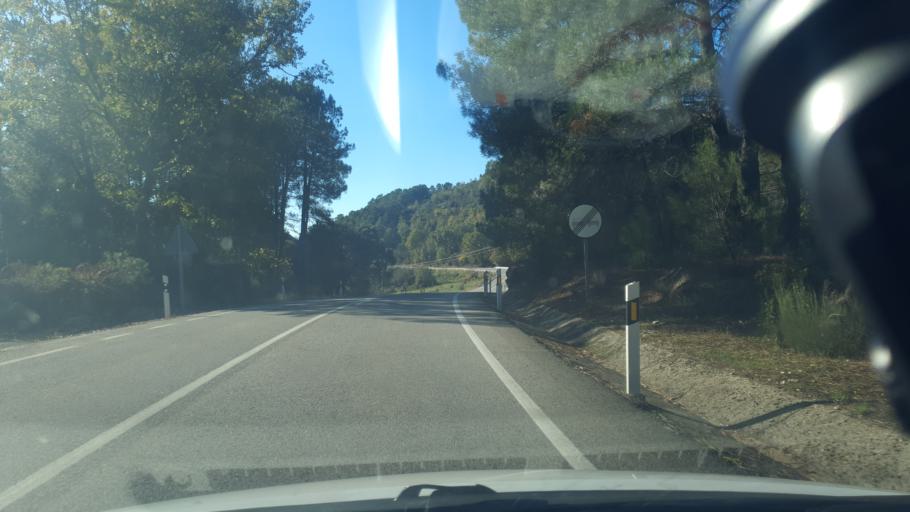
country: ES
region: Castille and Leon
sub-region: Provincia de Avila
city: Arenas de San Pedro
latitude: 40.2083
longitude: -5.0409
